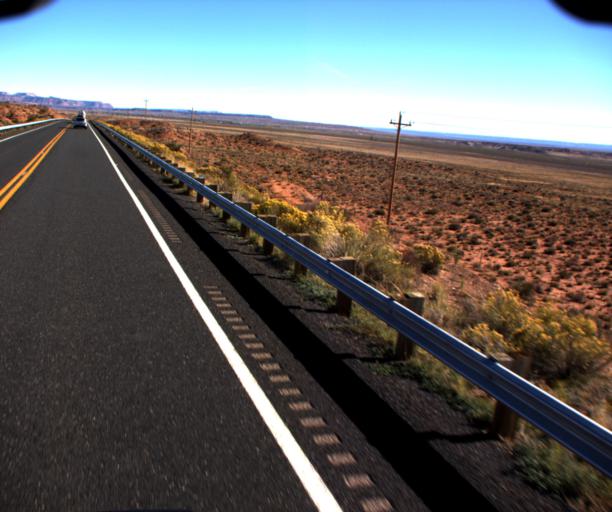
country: US
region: Arizona
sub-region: Coconino County
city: Fredonia
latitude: 36.9053
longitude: -112.5936
